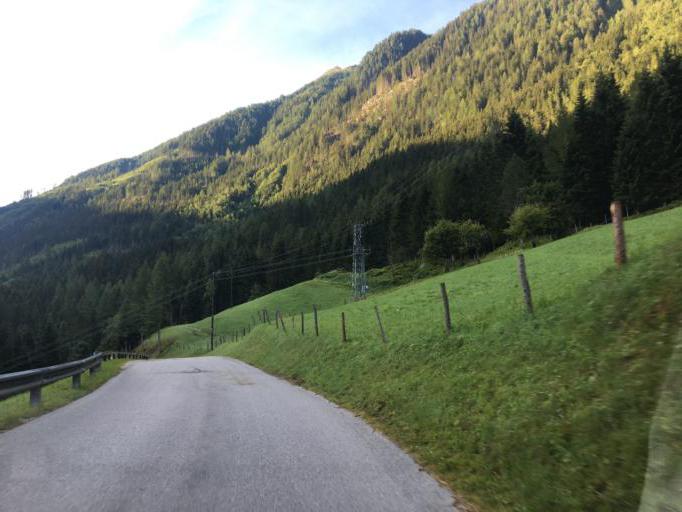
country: AT
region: Styria
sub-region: Politischer Bezirk Liezen
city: Schladming
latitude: 47.3590
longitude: 13.6913
